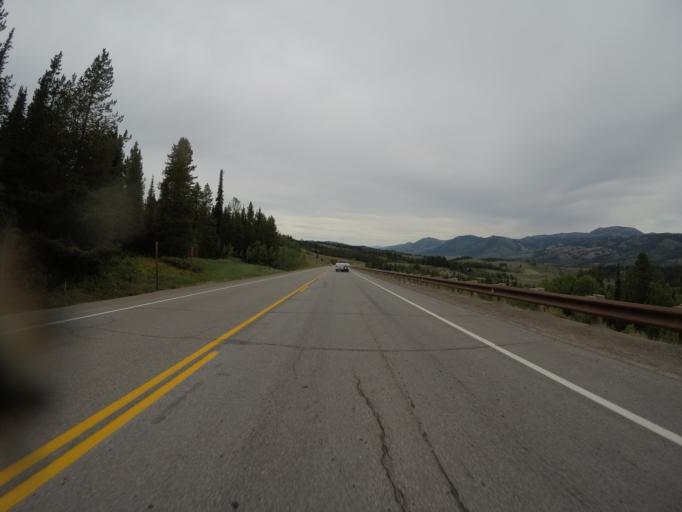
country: US
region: Wyoming
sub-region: Lincoln County
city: Afton
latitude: 42.5085
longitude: -110.9090
